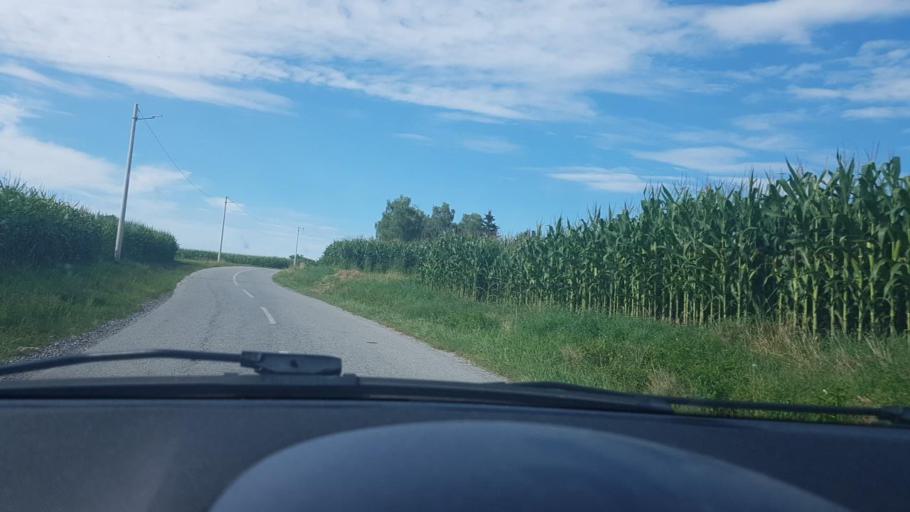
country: HR
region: Varazdinska
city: Tuzno
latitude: 46.2472
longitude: 16.1756
